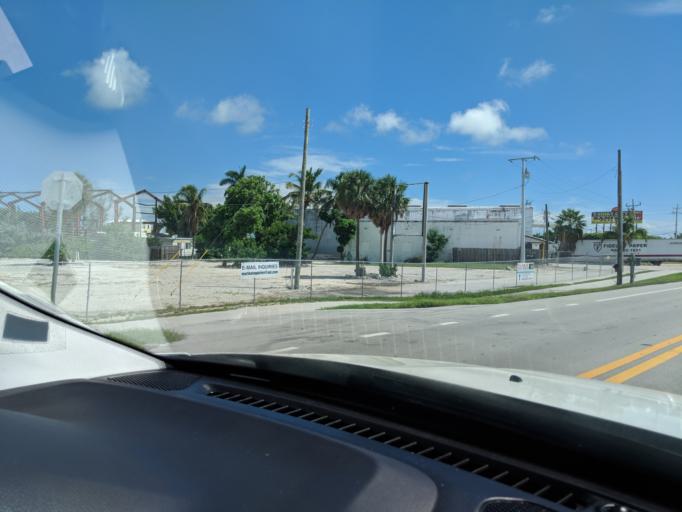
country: US
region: Florida
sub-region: Monroe County
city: Marathon
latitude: 24.7078
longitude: -81.1170
